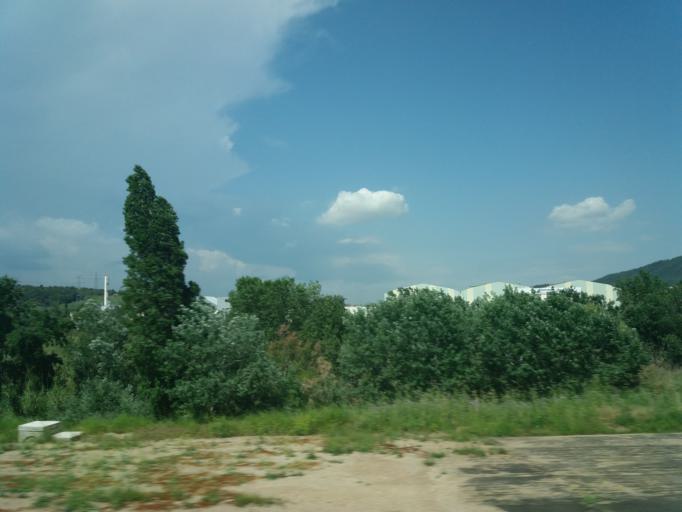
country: ES
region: Catalonia
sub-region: Provincia de Barcelona
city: Sant Andreu de la Barca
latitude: 41.4405
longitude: 1.9876
